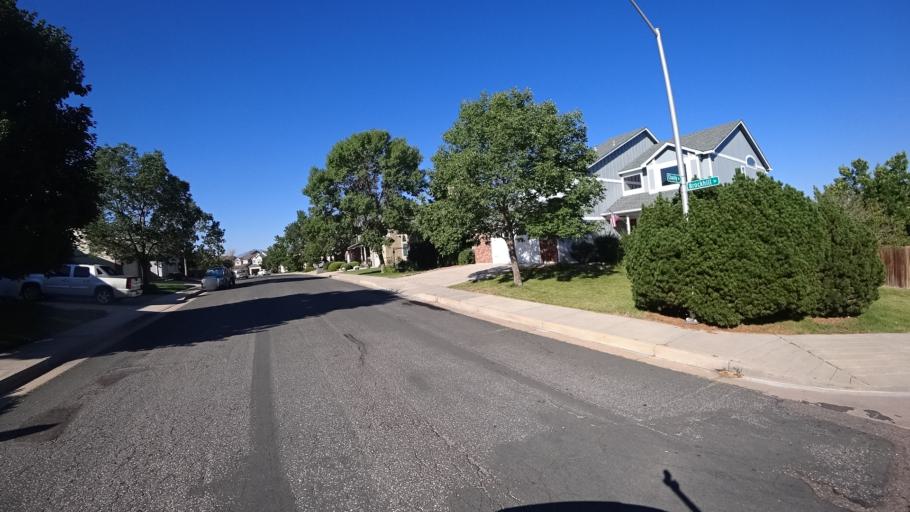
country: US
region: Colorado
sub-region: El Paso County
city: Black Forest
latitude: 38.9594
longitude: -104.7619
